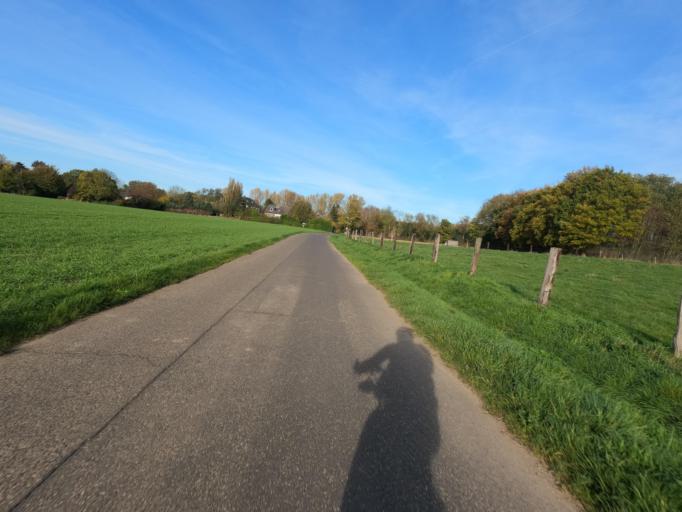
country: DE
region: North Rhine-Westphalia
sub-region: Regierungsbezirk Koln
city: Titz
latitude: 51.0801
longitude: 6.4000
